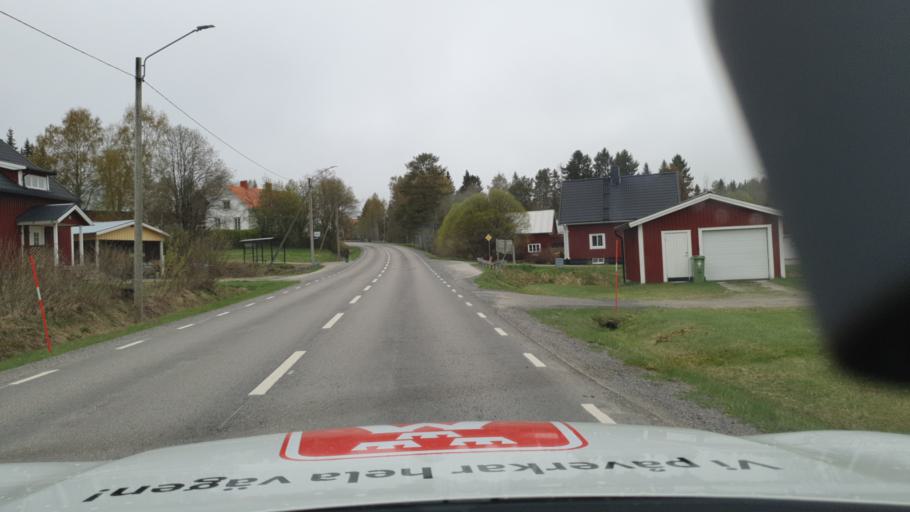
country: SE
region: Vaesterbotten
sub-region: Vannas Kommun
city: Vaennaes
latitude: 63.7823
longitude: 19.8412
